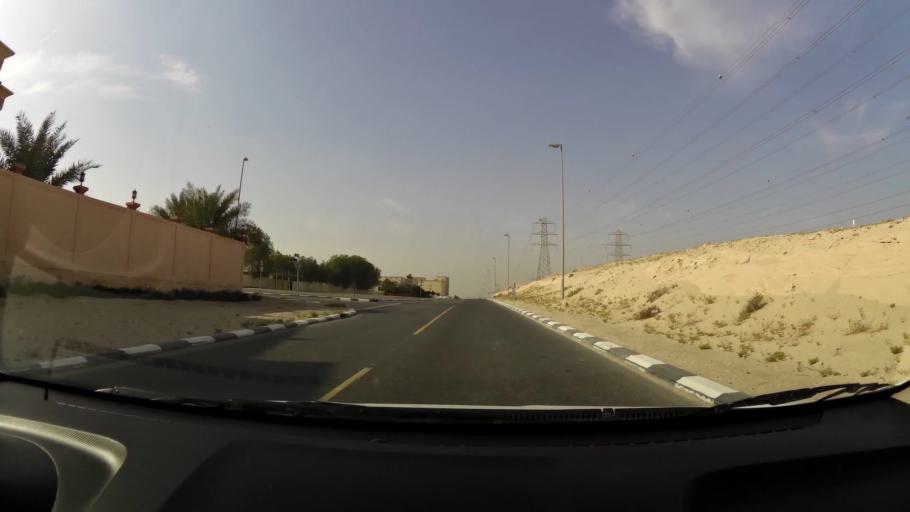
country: AE
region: Ash Shariqah
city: Sharjah
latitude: 25.2424
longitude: 55.4067
